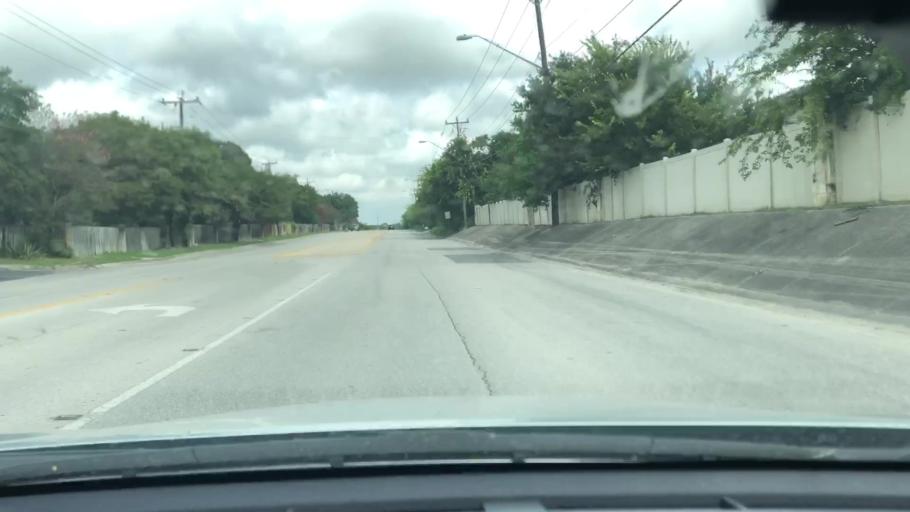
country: US
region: Texas
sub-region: Bexar County
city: Windcrest
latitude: 29.5219
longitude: -98.3692
